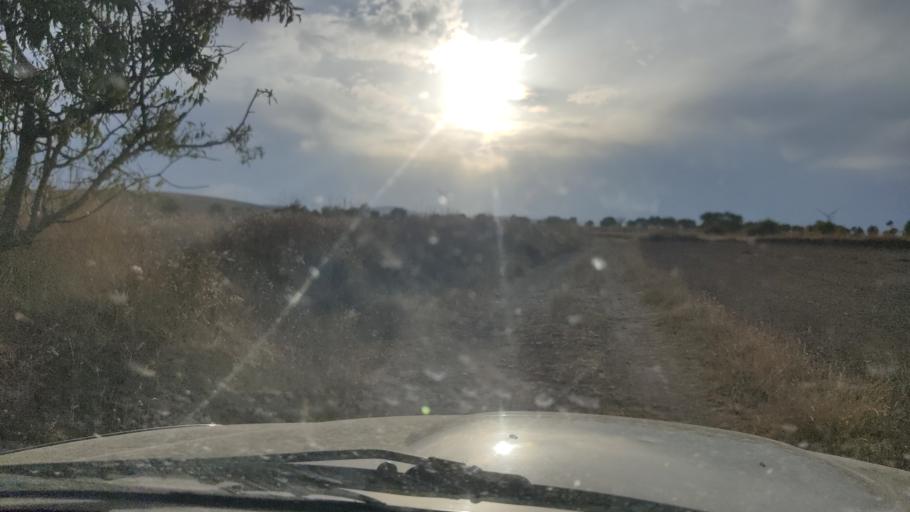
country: ES
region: Aragon
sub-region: Provincia de Teruel
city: Monforte de Moyuela
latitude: 41.0660
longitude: -0.9808
